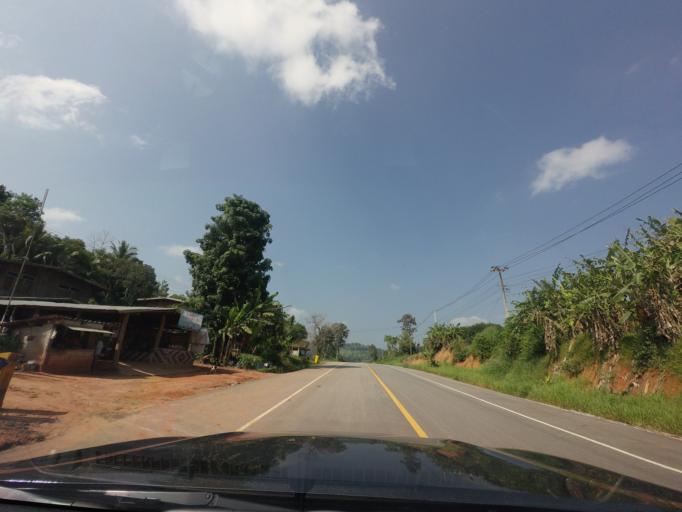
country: TH
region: Loei
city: Na Haeo
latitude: 17.4969
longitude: 101.0329
